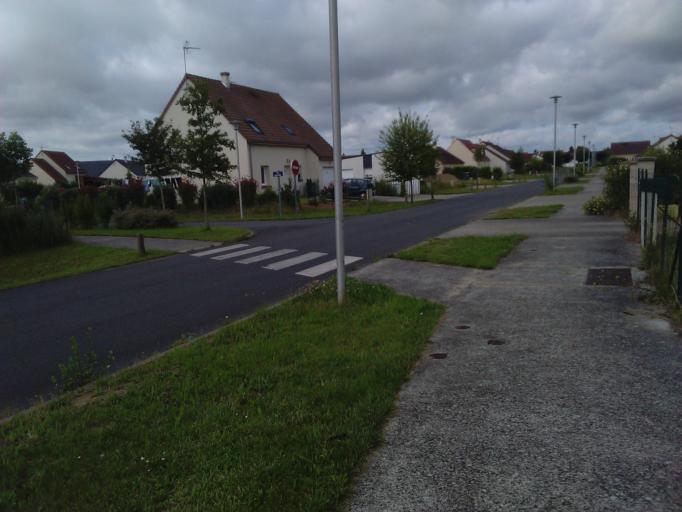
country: FR
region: Centre
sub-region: Departement du Loir-et-Cher
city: Naveil
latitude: 47.7907
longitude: 1.0380
